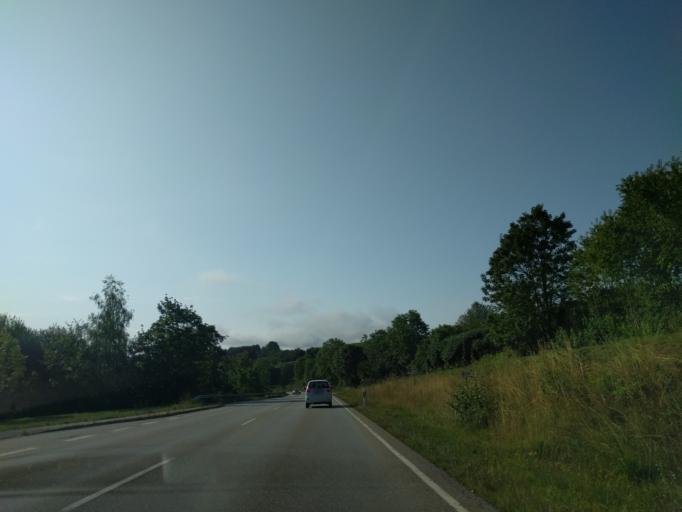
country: DE
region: Bavaria
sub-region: Lower Bavaria
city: Grafenau
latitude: 48.8306
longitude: 13.3482
